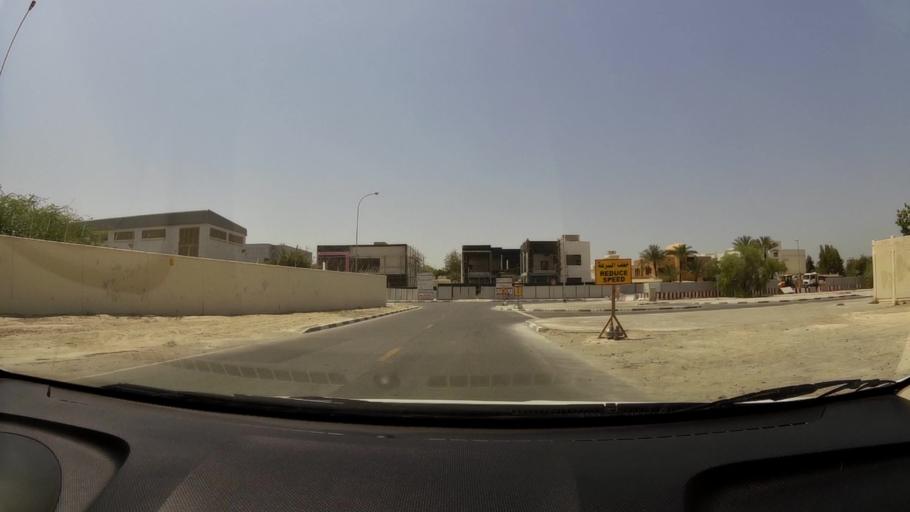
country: AE
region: Ash Shariqah
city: Sharjah
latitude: 25.2946
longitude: 55.3437
